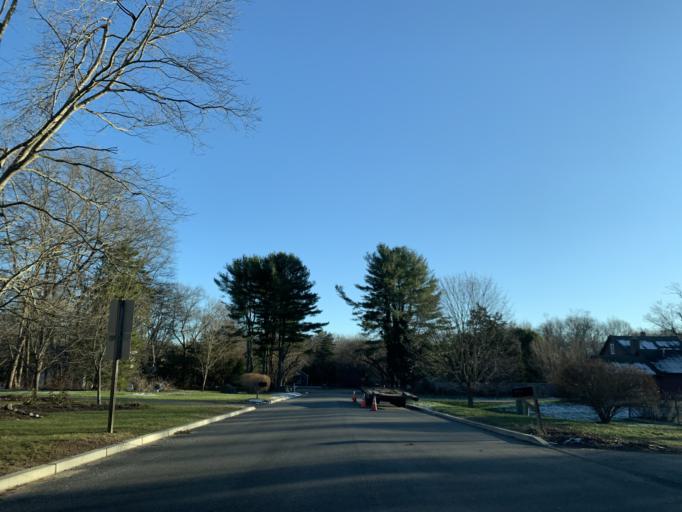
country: US
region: Rhode Island
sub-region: Washington County
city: Exeter
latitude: 41.6253
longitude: -71.5183
